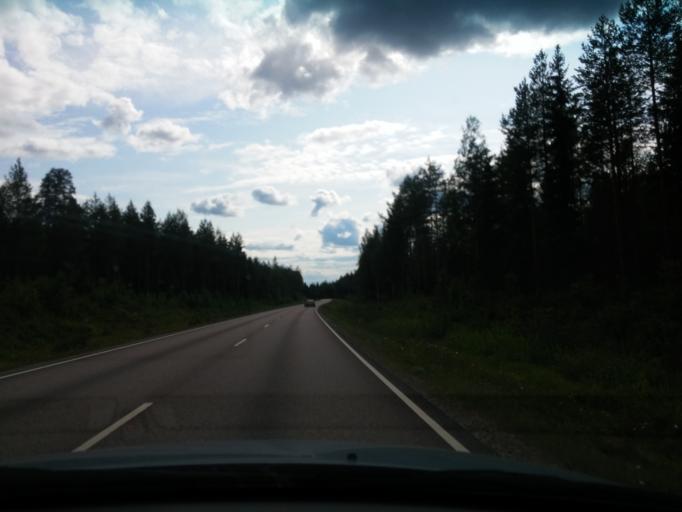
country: FI
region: Central Finland
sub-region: Keuruu
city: Multia
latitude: 62.3813
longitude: 24.7508
